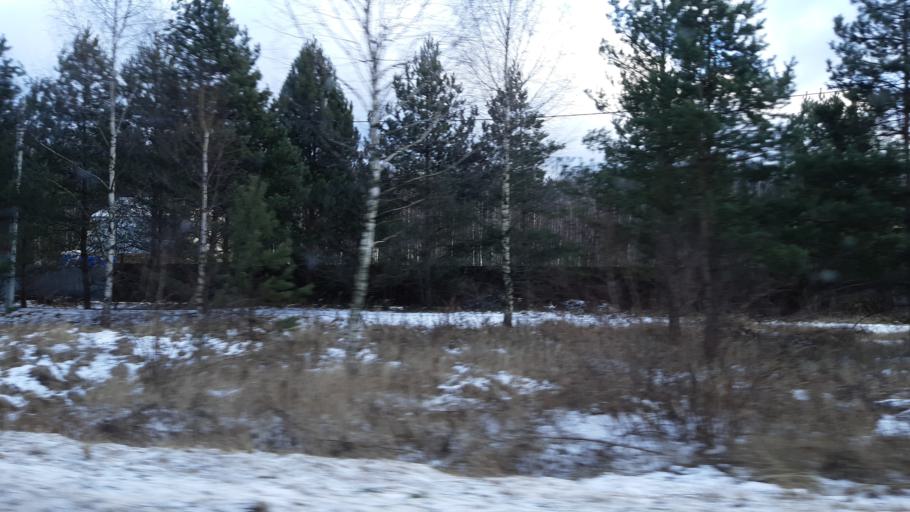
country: RU
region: Moskovskaya
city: Noginsk-9
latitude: 55.9983
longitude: 38.5455
